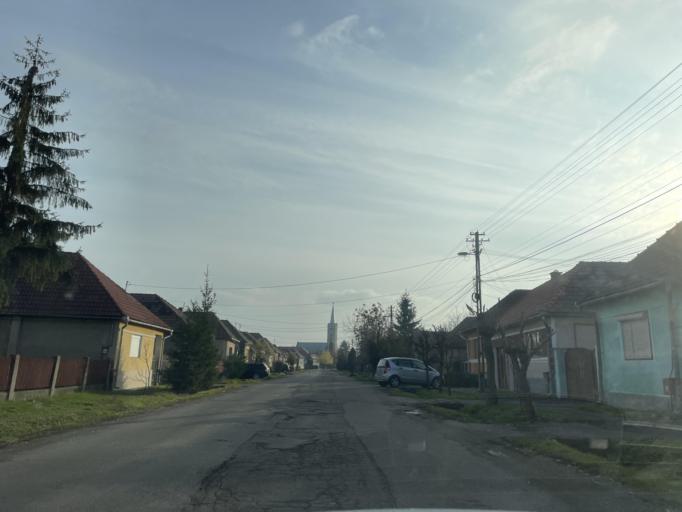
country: RO
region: Mures
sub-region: Municipiul Reghin
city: Apalina
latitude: 46.7494
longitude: 24.6937
